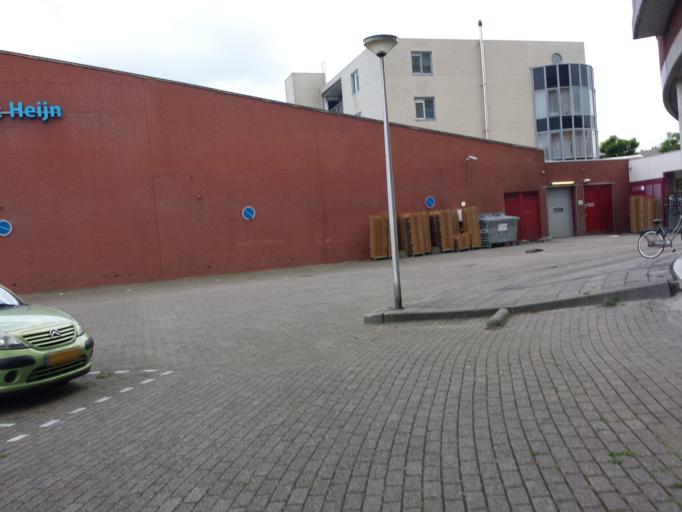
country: NL
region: South Holland
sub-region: Gemeente Vlist
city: Haastrecht
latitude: 52.0119
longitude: 4.7437
